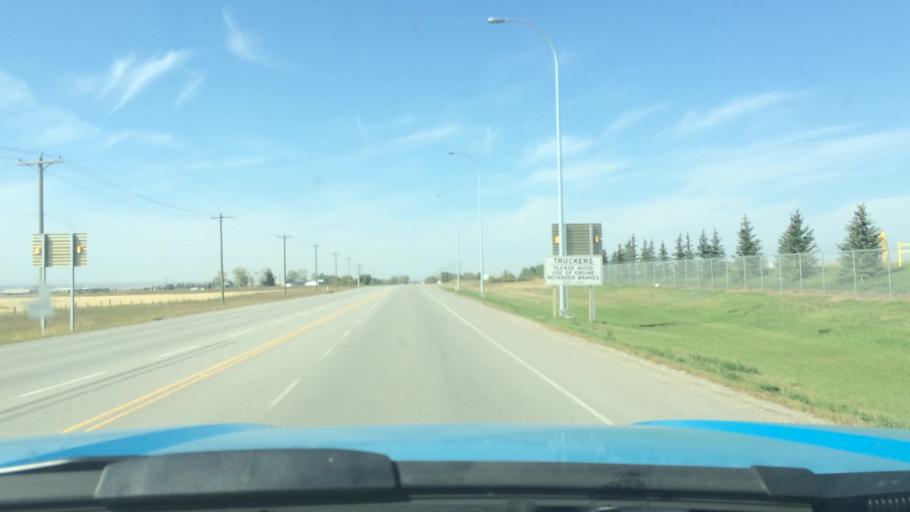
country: CA
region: Alberta
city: Airdrie
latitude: 51.2135
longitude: -113.9385
